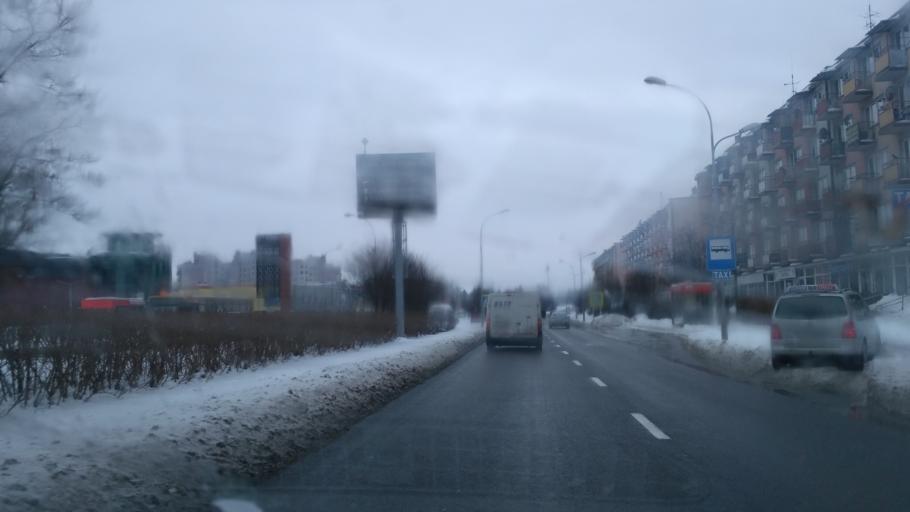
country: PL
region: Subcarpathian Voivodeship
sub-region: Rzeszow
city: Rzeszow
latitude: 50.0490
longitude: 21.9872
